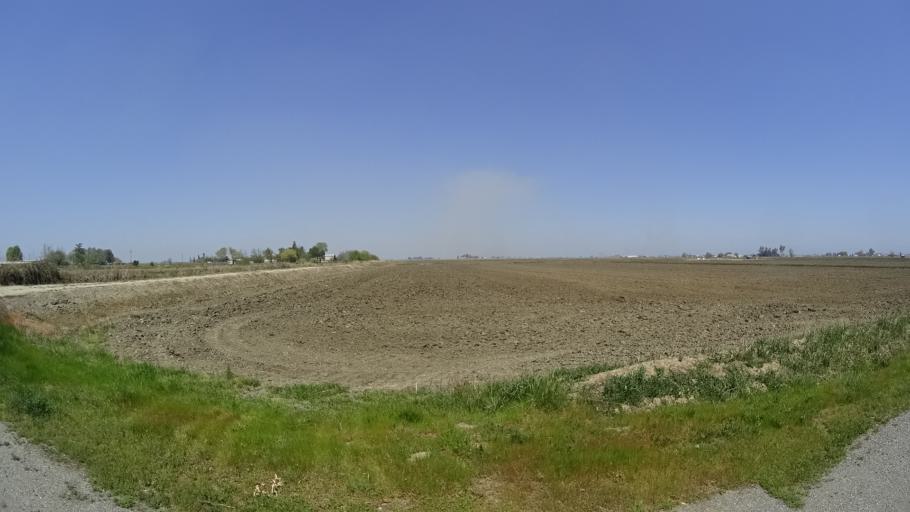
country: US
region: California
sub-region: Glenn County
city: Willows
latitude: 39.5505
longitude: -122.1004
